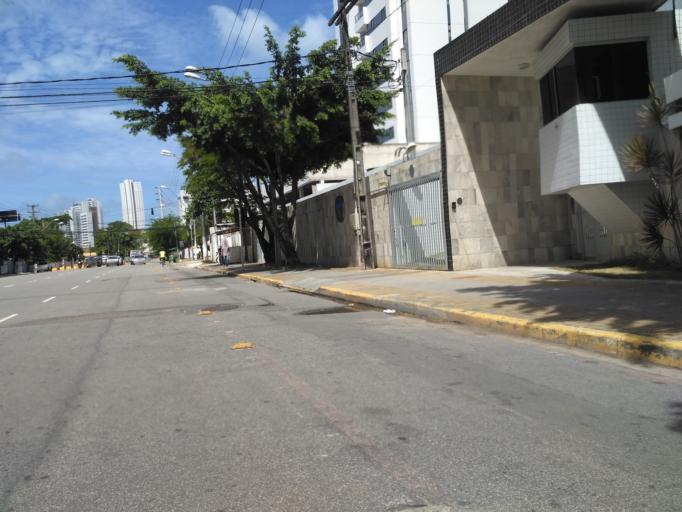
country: BR
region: Pernambuco
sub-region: Recife
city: Recife
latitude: -8.0863
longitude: -34.8895
